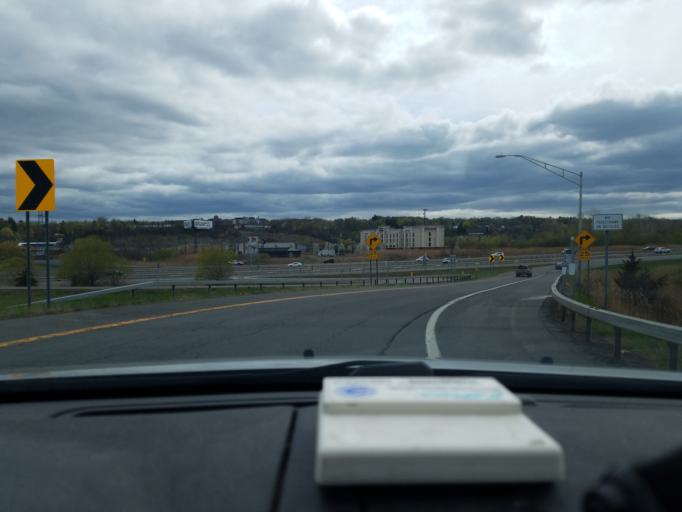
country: US
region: New York
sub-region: Onondaga County
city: East Syracuse
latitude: 43.0599
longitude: -76.0846
